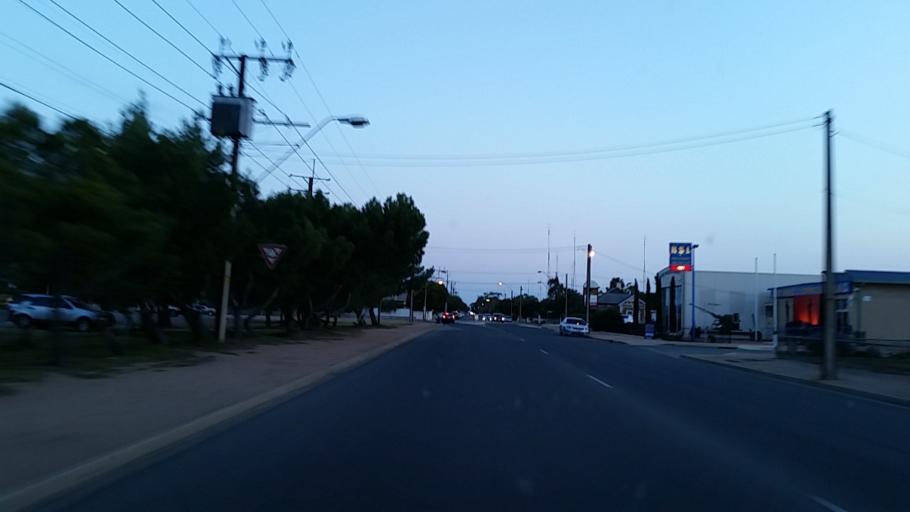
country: AU
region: South Australia
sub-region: Port Pirie City and Dists
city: Port Pirie
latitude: -33.1882
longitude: 138.0039
